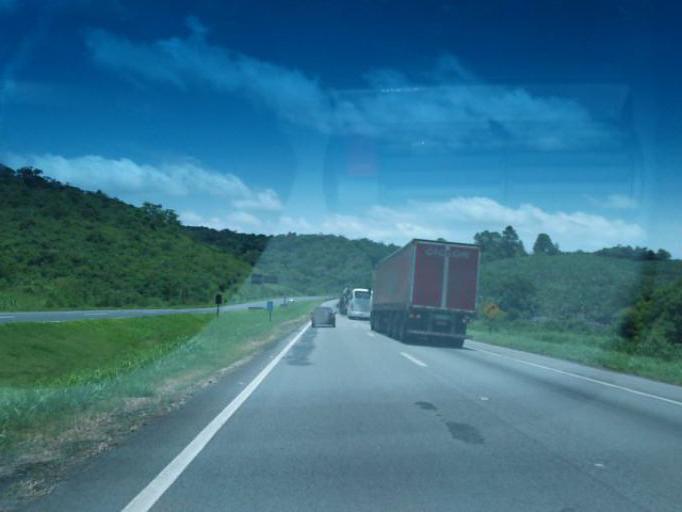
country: BR
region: Sao Paulo
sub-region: Juquia
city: Juquia
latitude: -24.3967
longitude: -47.7287
